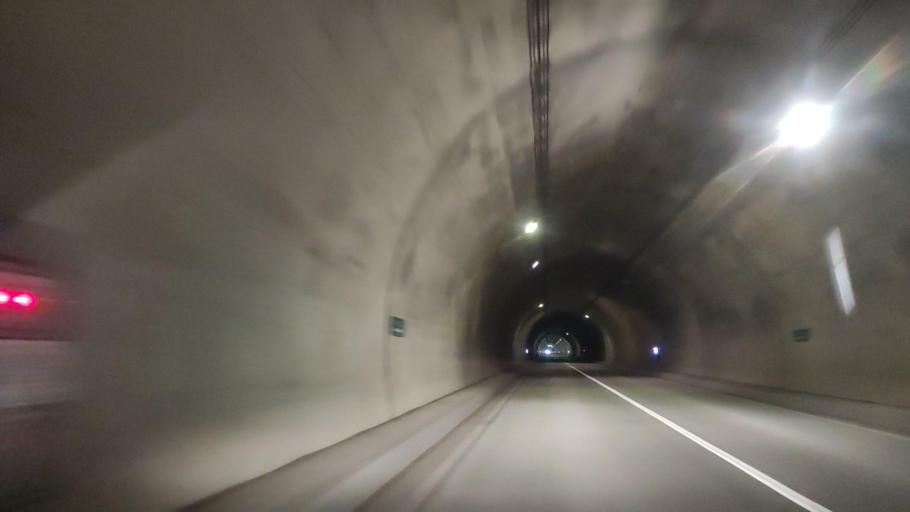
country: JP
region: Hokkaido
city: Iwamizawa
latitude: 43.0260
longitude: 142.0870
